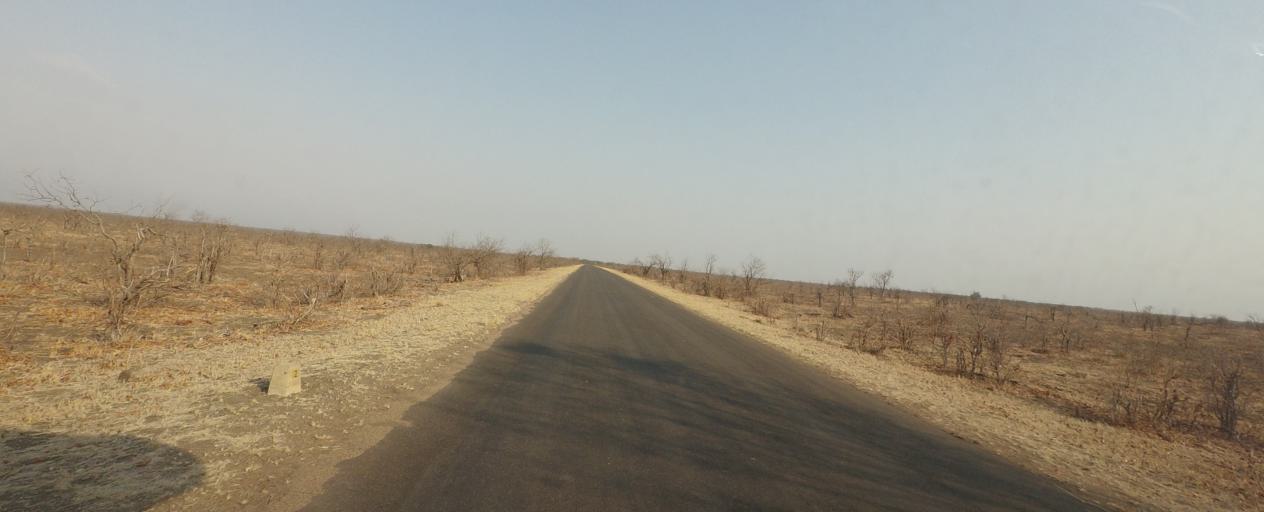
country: ZA
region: Limpopo
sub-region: Mopani District Municipality
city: Giyani
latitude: -23.0786
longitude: 31.4135
